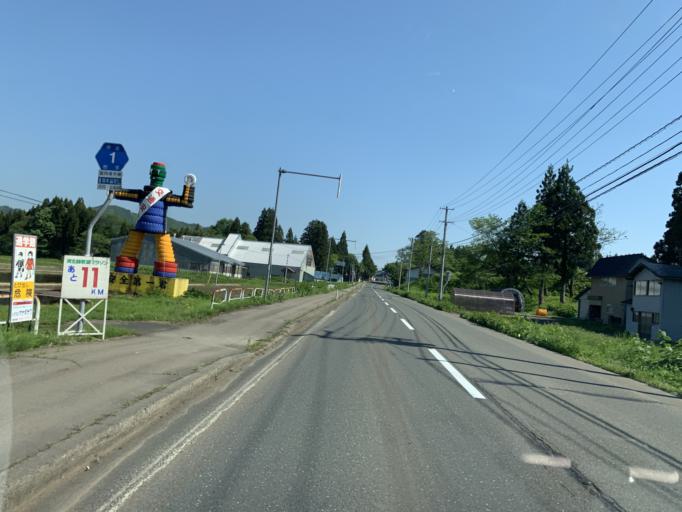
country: JP
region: Akita
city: Yokotemachi
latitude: 39.4020
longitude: 140.7551
